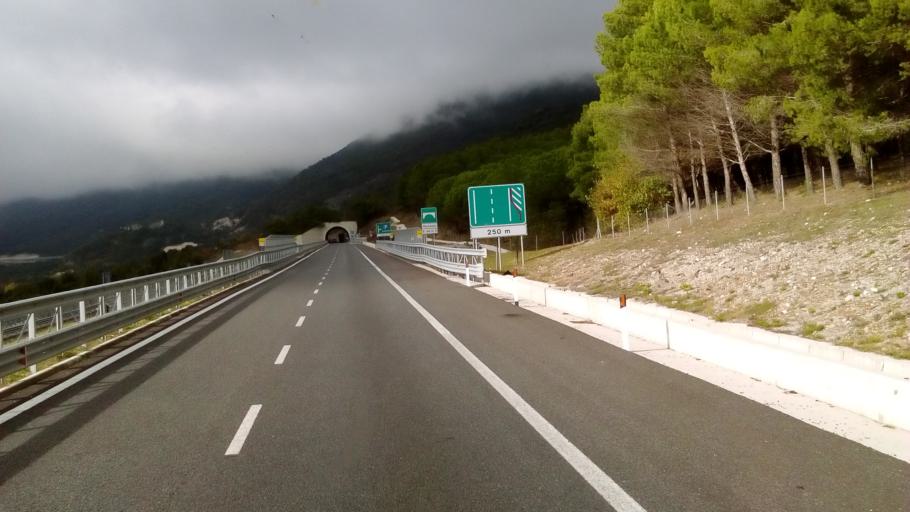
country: IT
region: Calabria
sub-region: Provincia di Cosenza
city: Morano Calabro
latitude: 39.8799
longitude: 16.1635
